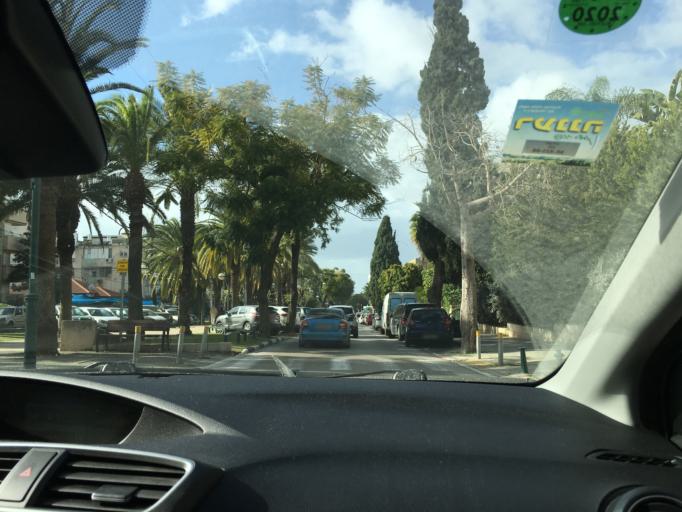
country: IL
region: Tel Aviv
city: Ramat HaSharon
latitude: 32.1455
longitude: 34.8403
